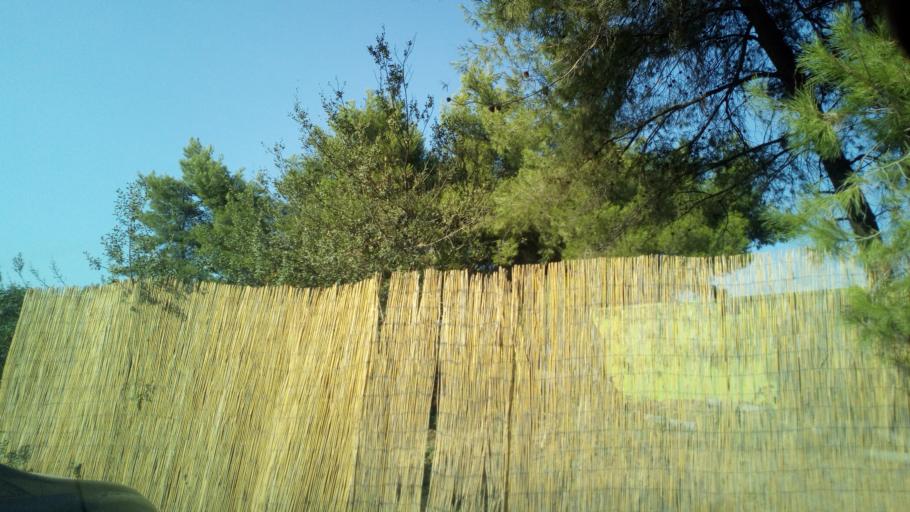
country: GR
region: Central Macedonia
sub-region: Nomos Chalkidikis
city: Pefkochori
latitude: 39.9575
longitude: 23.6789
